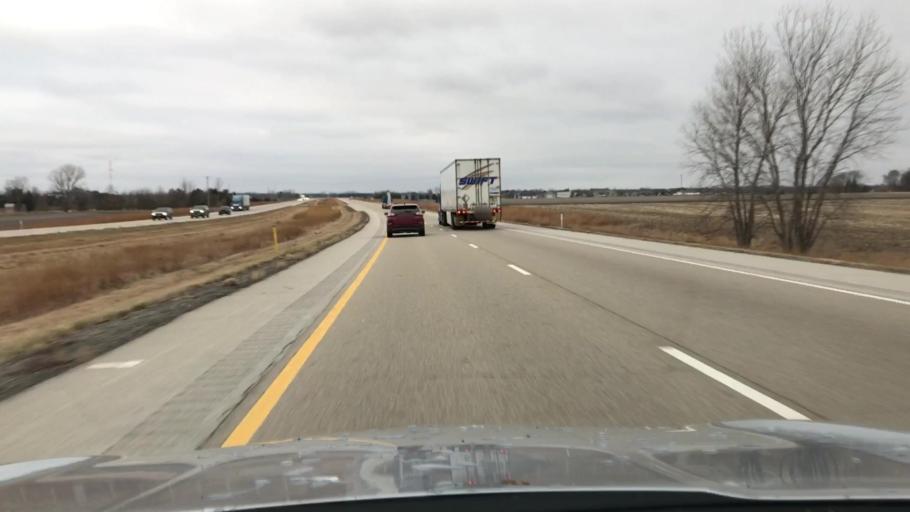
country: US
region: Illinois
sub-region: Logan County
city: Lincoln
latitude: 40.1853
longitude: -89.3263
